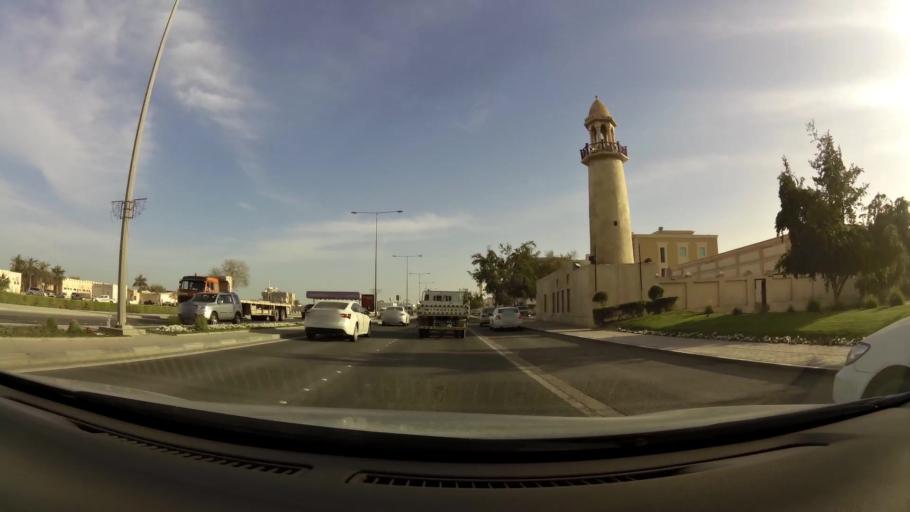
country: QA
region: Al Wakrah
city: Al Wakrah
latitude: 25.1707
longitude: 51.6072
